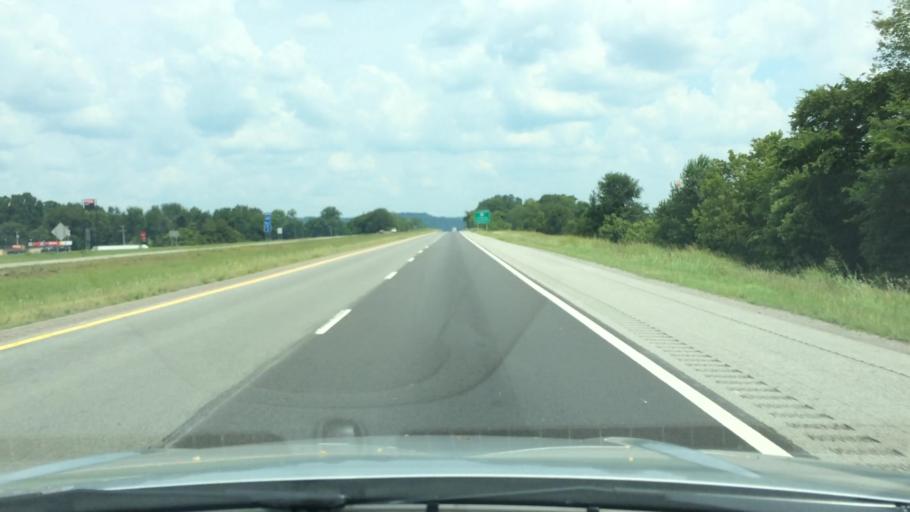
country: US
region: Tennessee
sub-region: Marshall County
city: Cornersville
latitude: 35.3024
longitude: -86.8824
